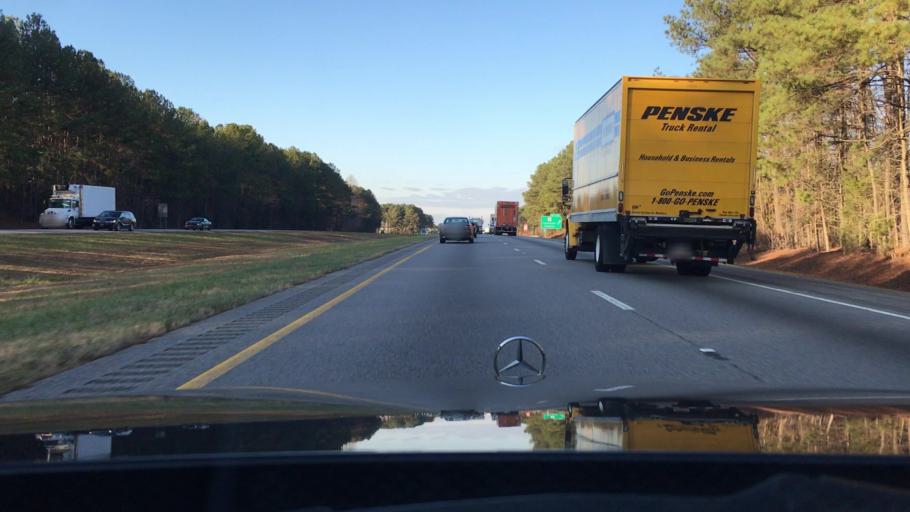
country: US
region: South Carolina
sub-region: Chester County
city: Eureka Mill
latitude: 34.7384
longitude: -81.0348
